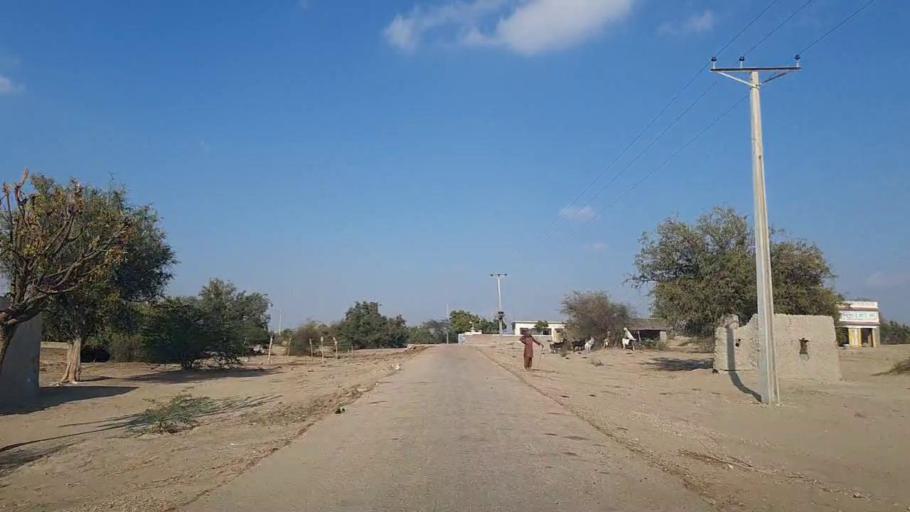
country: PK
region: Sindh
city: Tando Mittha Khan
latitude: 26.0153
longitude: 69.2491
